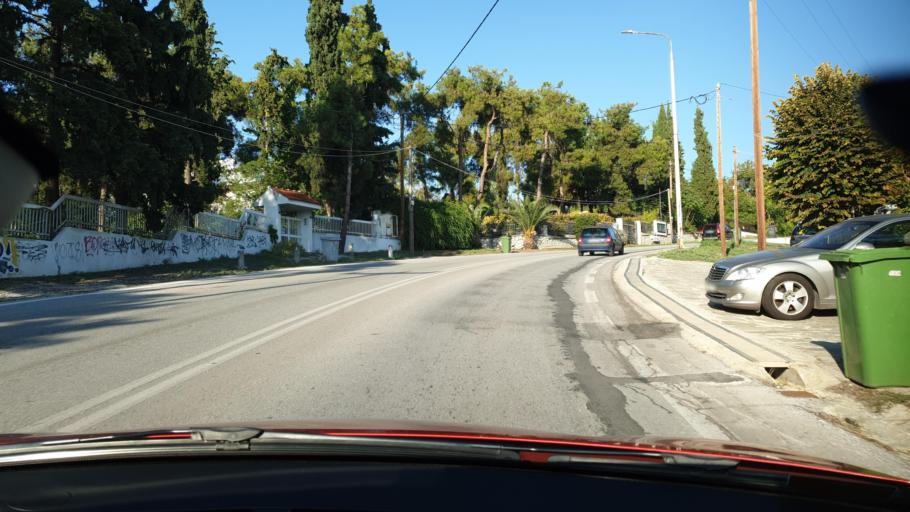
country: GR
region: Central Macedonia
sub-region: Nomos Thessalonikis
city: Panorama
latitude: 40.5920
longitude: 23.0201
